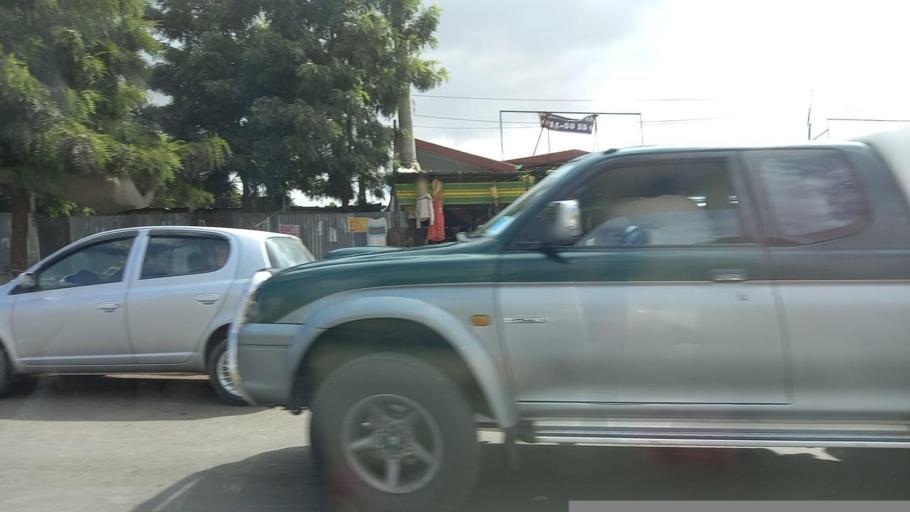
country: ET
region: Adis Abeba
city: Addis Ababa
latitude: 9.0208
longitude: 38.8645
